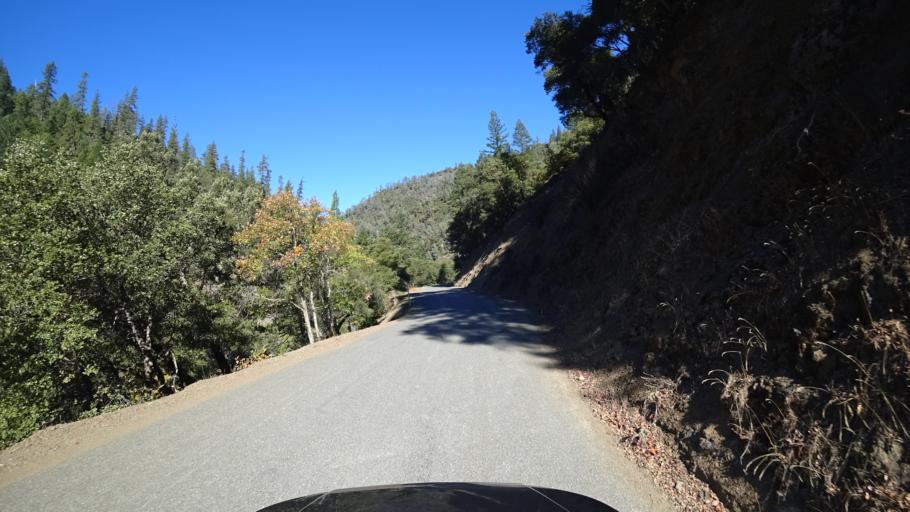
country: US
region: California
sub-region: Humboldt County
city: Willow Creek
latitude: 41.2068
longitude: -123.2281
